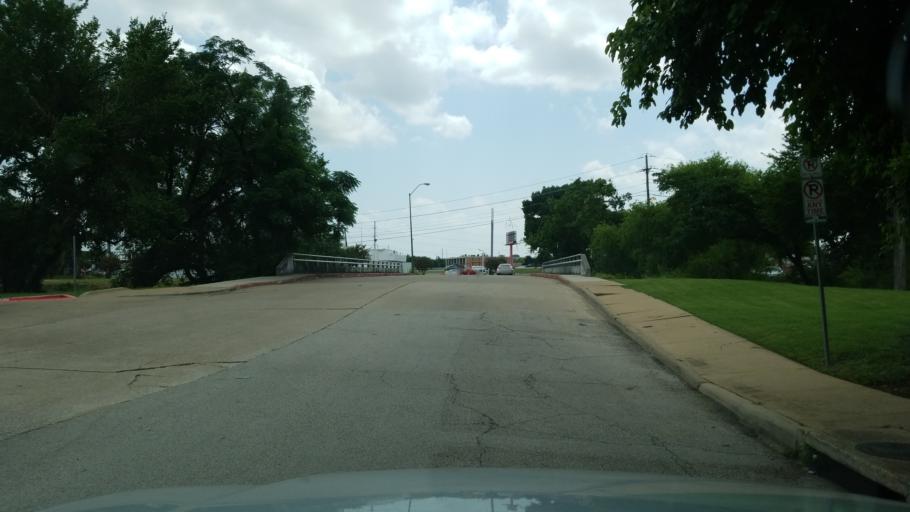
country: US
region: Texas
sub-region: Dallas County
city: Dallas
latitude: 32.8162
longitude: -96.8652
